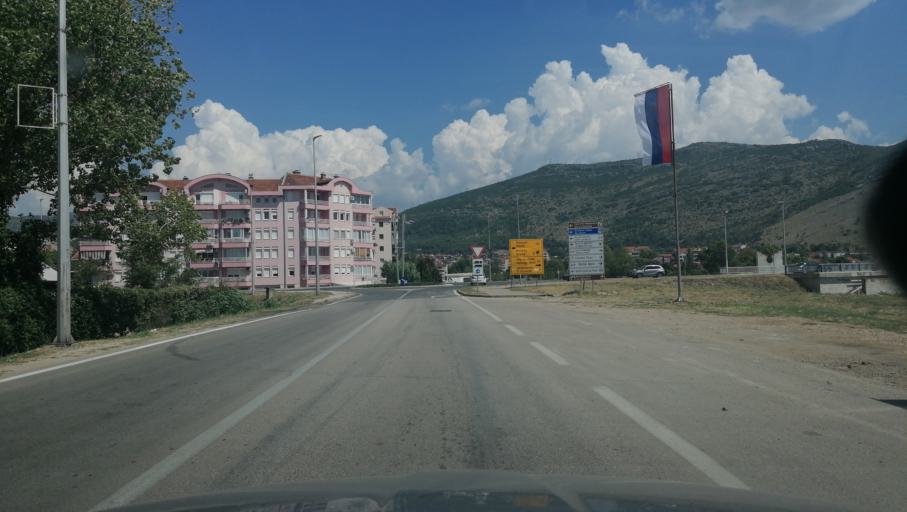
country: BA
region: Republika Srpska
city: Trebinje
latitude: 42.7055
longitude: 18.3420
